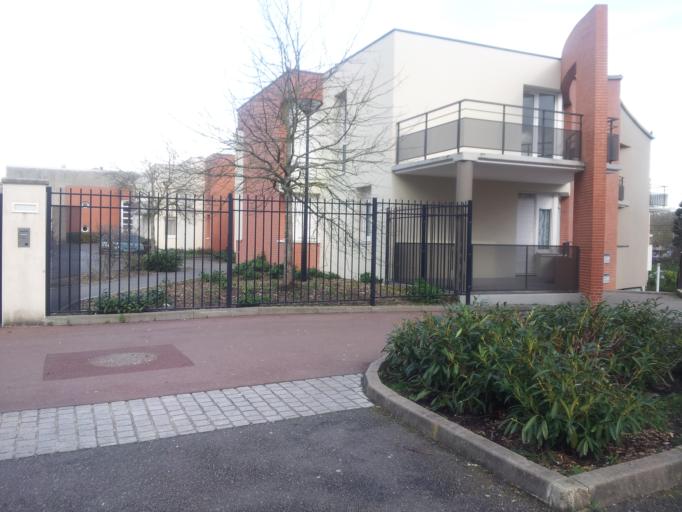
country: FR
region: Centre
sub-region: Departement du Loiret
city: Saint-Cyr-en-Val
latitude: 47.8387
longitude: 1.9337
